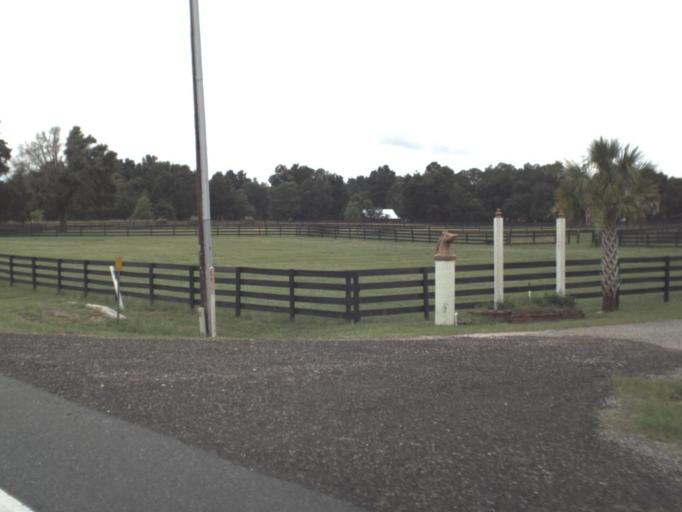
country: US
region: Florida
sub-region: Levy County
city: Williston
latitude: 29.3031
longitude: -82.4492
